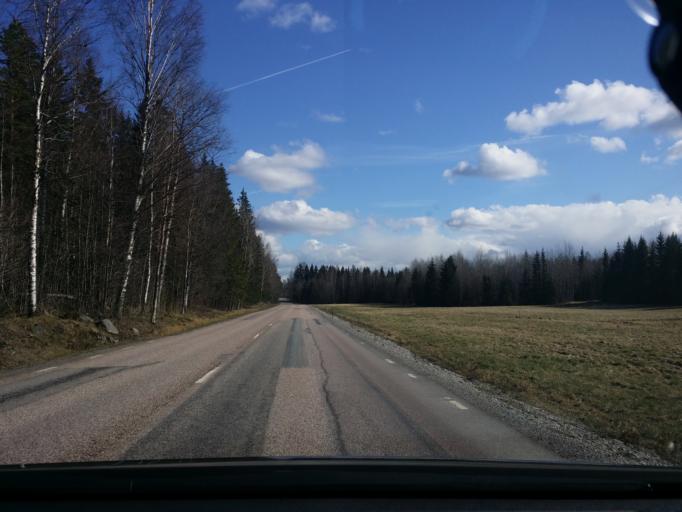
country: SE
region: Vaestmanland
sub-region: Sala Kommun
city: Sala
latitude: 59.9785
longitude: 16.4925
